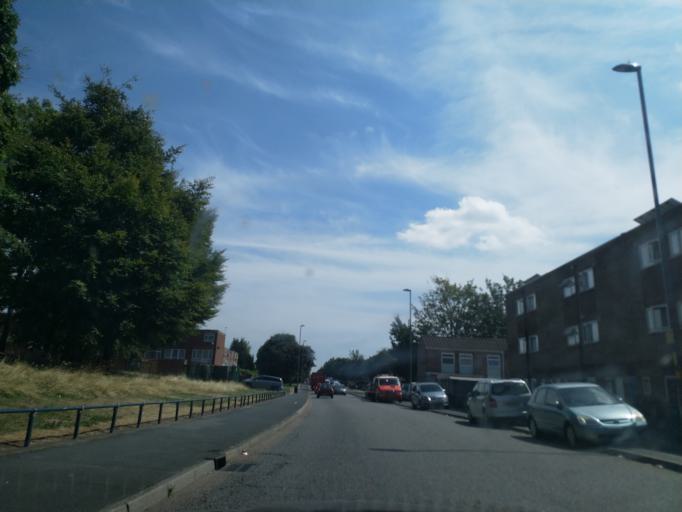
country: GB
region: England
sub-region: City and Borough of Birmingham
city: Birmingham
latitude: 52.4993
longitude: -1.8914
